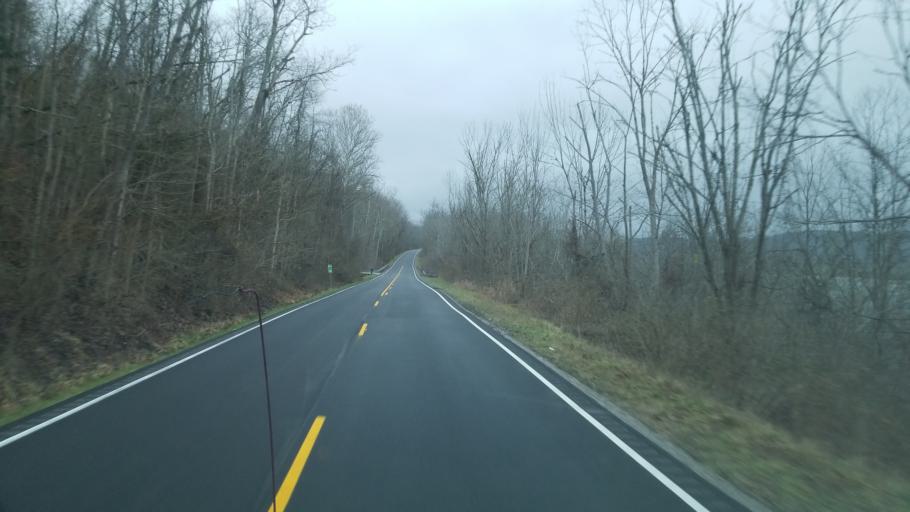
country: US
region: Kentucky
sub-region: Bracken County
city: Augusta
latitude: 38.7661
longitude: -83.9246
